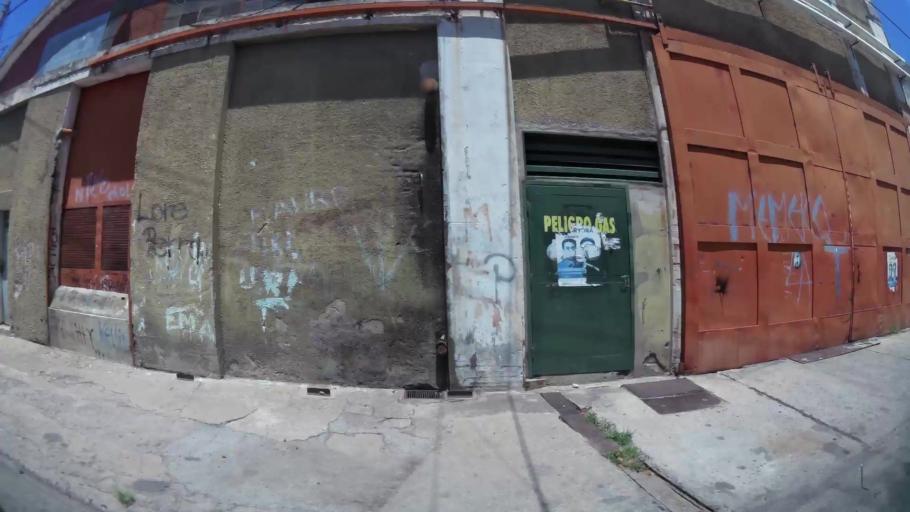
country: AR
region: Cordoba
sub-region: Departamento de Capital
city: Cordoba
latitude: -31.3935
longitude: -64.2082
